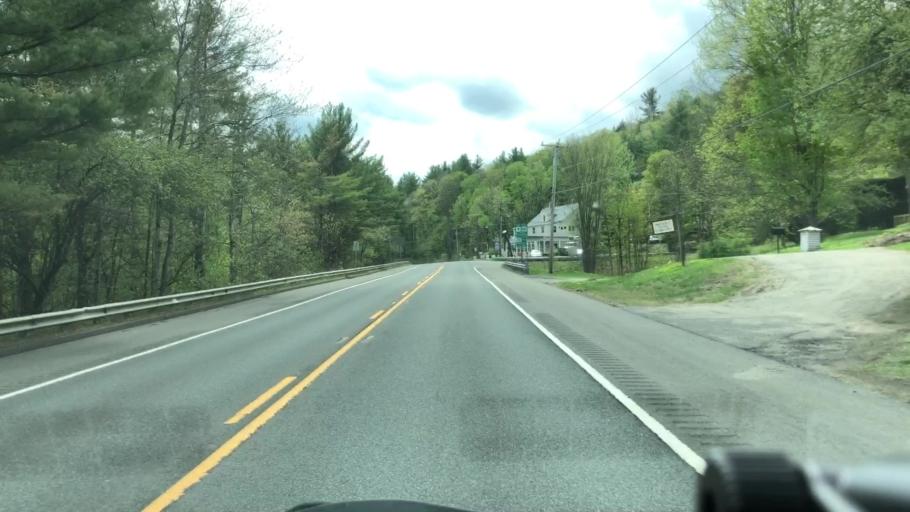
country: US
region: Massachusetts
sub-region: Hampshire County
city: Chesterfield
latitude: 42.4655
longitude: -72.9057
